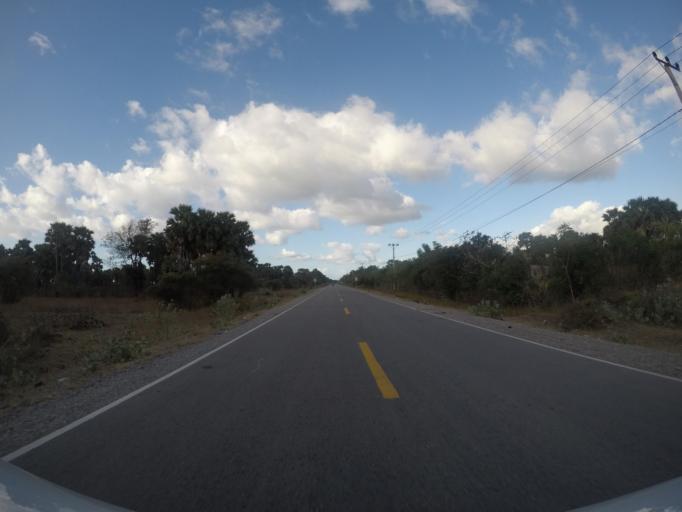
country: TL
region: Lautem
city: Lospalos
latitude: -8.3854
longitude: 126.8565
